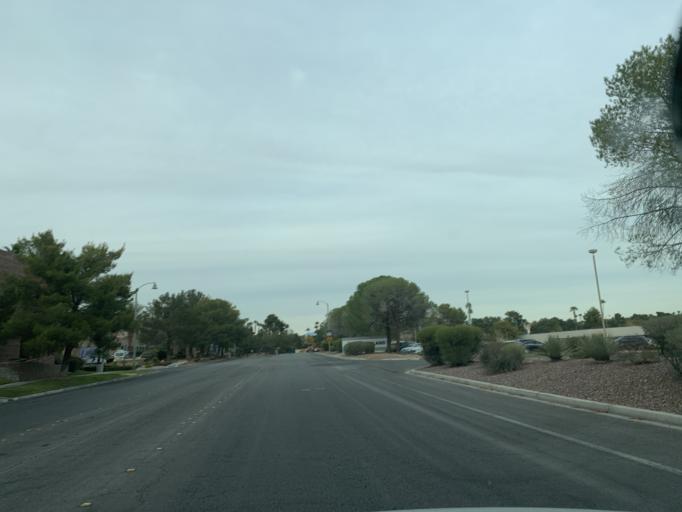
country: US
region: Nevada
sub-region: Clark County
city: Summerlin South
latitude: 36.1424
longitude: -115.2879
